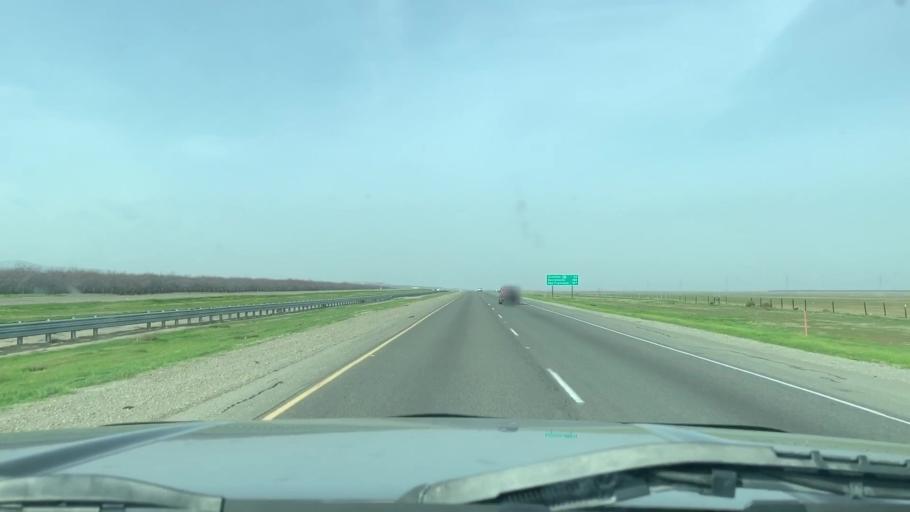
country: US
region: California
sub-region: Fresno County
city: San Joaquin
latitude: 36.4455
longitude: -120.4028
